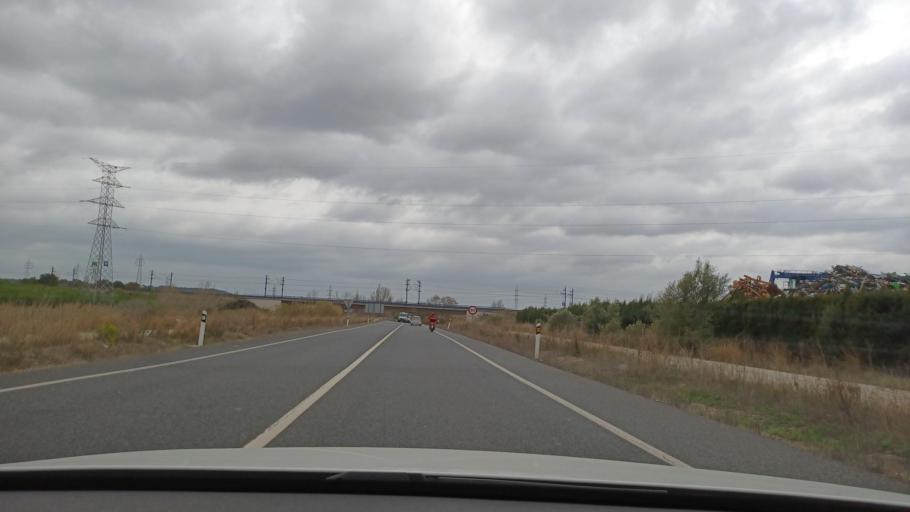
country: ES
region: Catalonia
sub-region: Provincia de Tarragona
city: la Pobla de Mafumet
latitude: 41.2007
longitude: 1.2432
